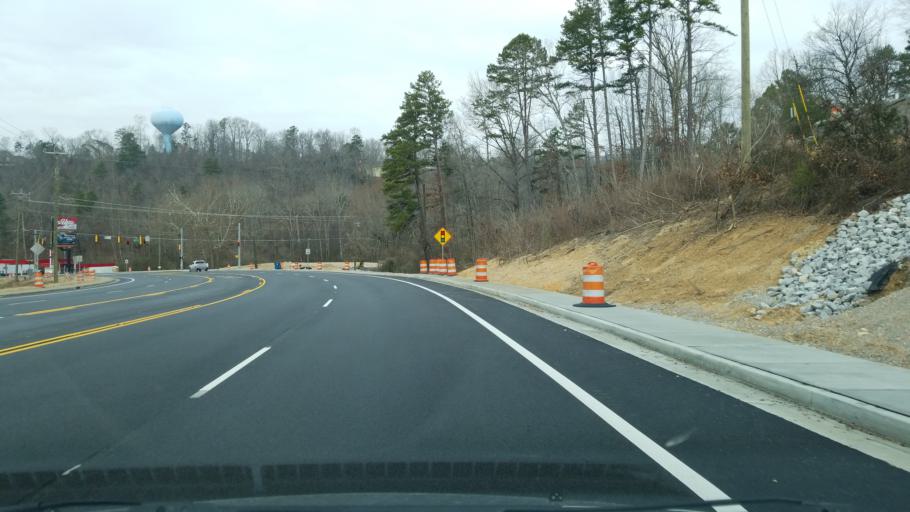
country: US
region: Tennessee
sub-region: Hamilton County
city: East Brainerd
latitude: 35.0052
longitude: -85.1189
